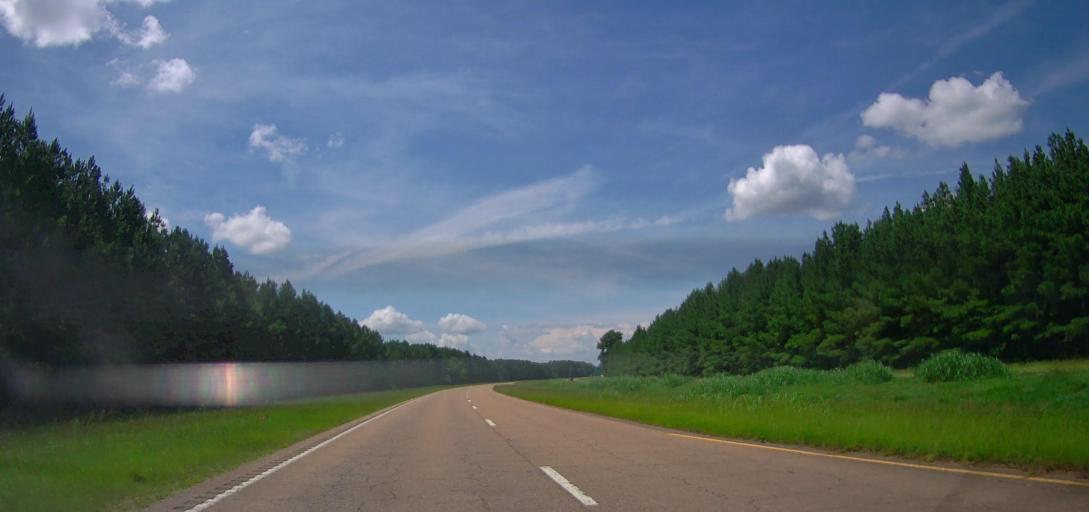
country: US
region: Mississippi
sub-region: Monroe County
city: Aberdeen
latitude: 33.8193
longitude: -88.5811
